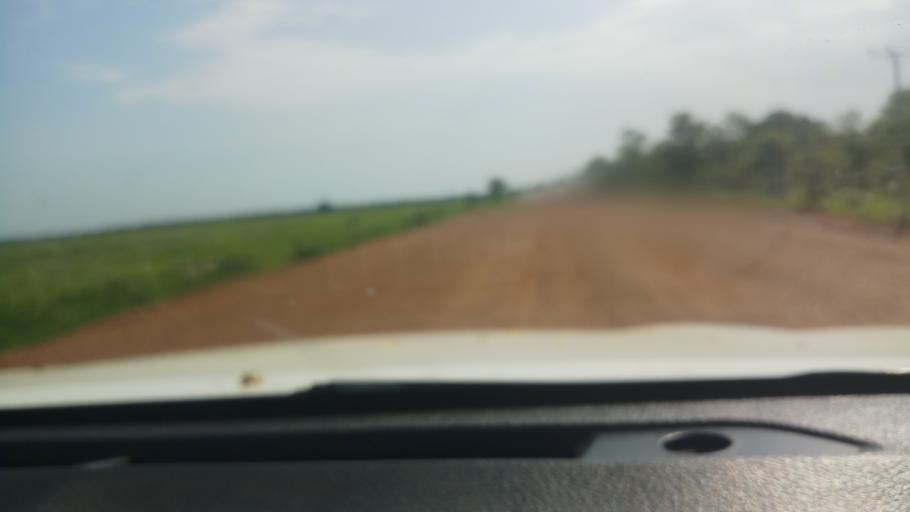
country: ET
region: Gambela
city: Gambela
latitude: 8.1632
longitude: 34.3216
